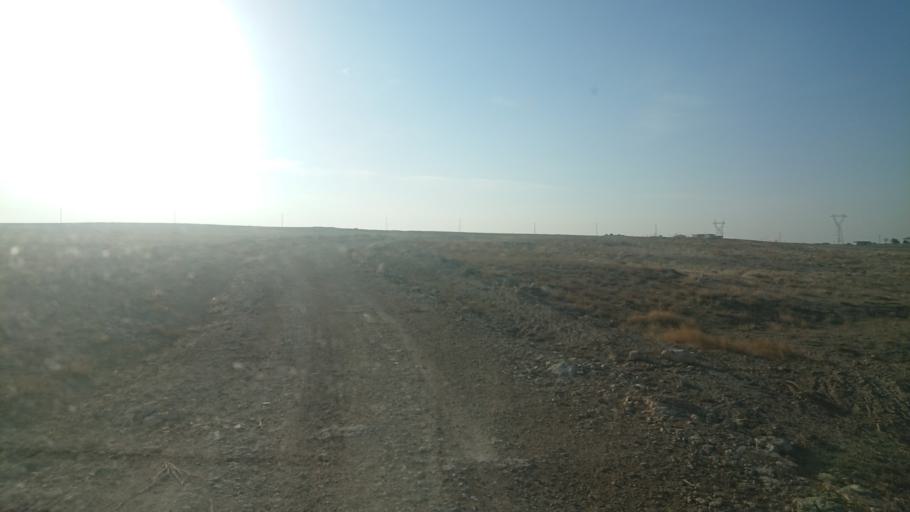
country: TR
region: Aksaray
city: Sultanhani
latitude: 38.1456
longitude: 33.5834
